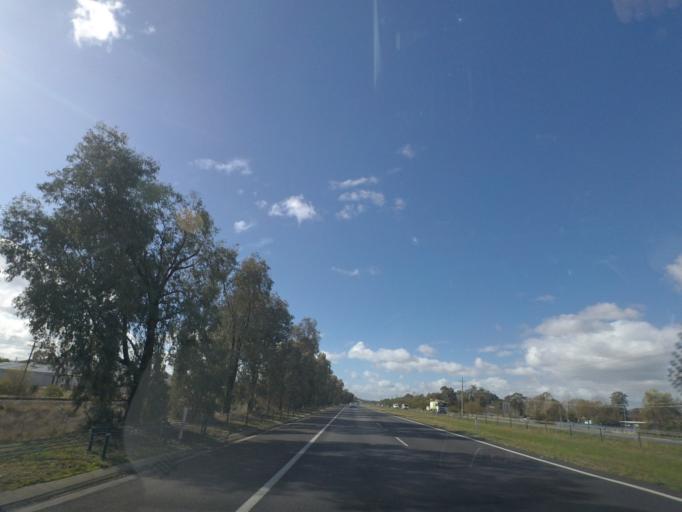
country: AU
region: New South Wales
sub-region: Albury Municipality
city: Lavington
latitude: -36.0591
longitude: 146.9486
